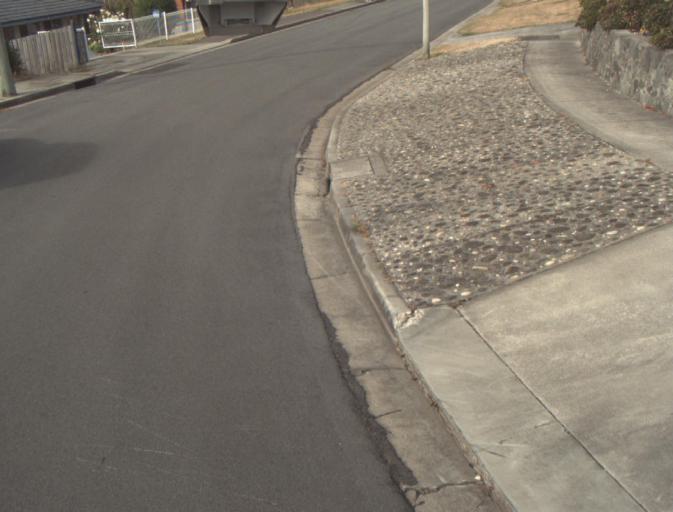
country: AU
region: Tasmania
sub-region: Launceston
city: Invermay
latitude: -41.3912
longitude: 147.1368
